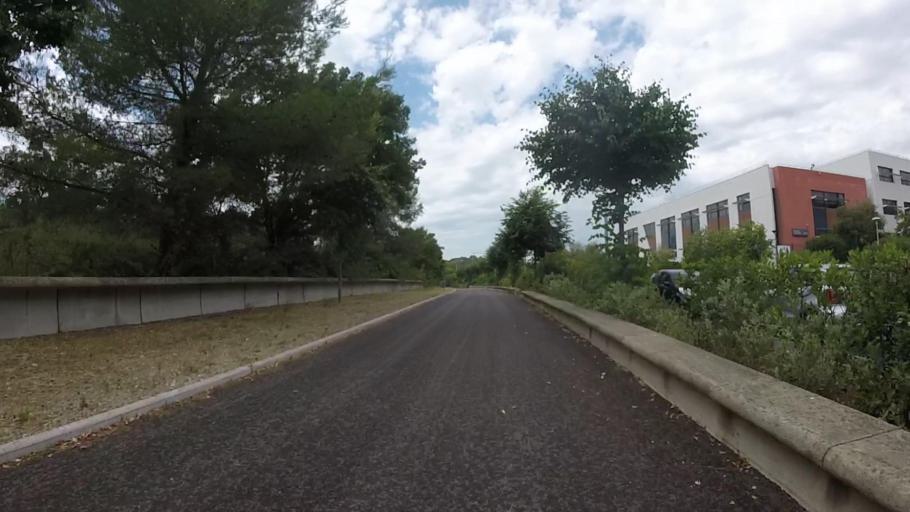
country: FR
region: Provence-Alpes-Cote d'Azur
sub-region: Departement des Alpes-Maritimes
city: Biot
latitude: 43.6230
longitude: 7.0705
